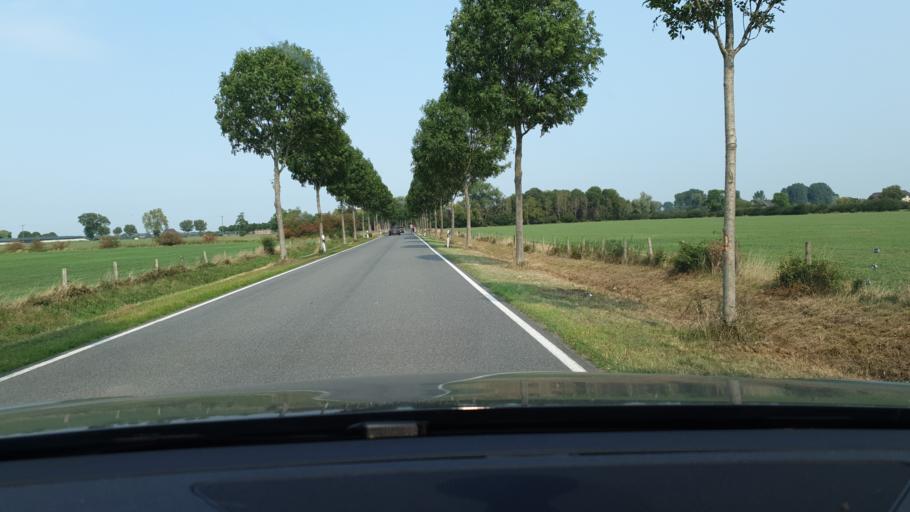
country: DE
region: North Rhine-Westphalia
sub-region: Regierungsbezirk Dusseldorf
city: Kranenburg
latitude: 51.8042
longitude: 6.0142
